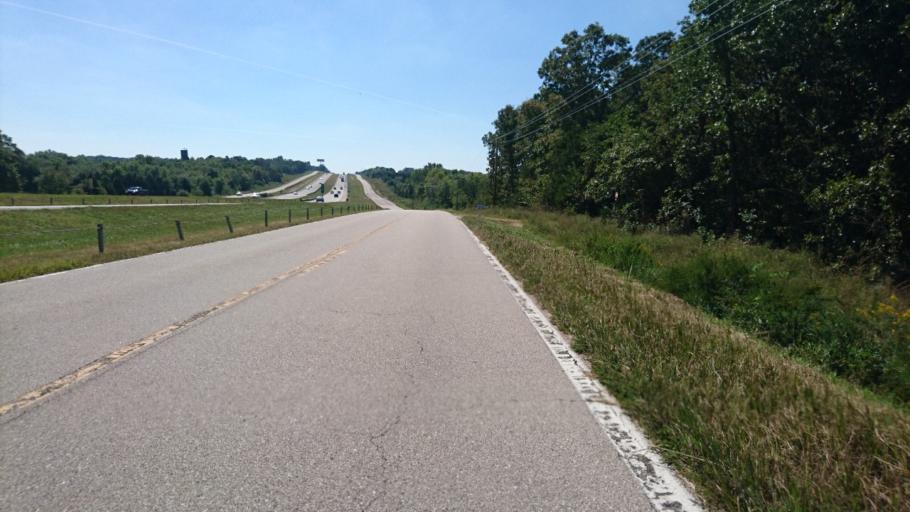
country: US
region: Missouri
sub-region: Franklin County
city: Sullivan
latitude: 38.2518
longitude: -91.1334
